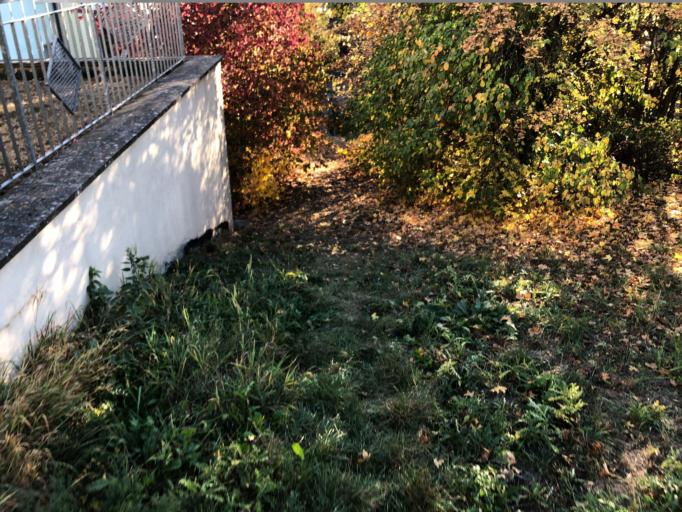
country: DE
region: Bavaria
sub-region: Regierungsbezirk Mittelfranken
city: Feuchtwangen
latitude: 49.1694
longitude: 10.3342
